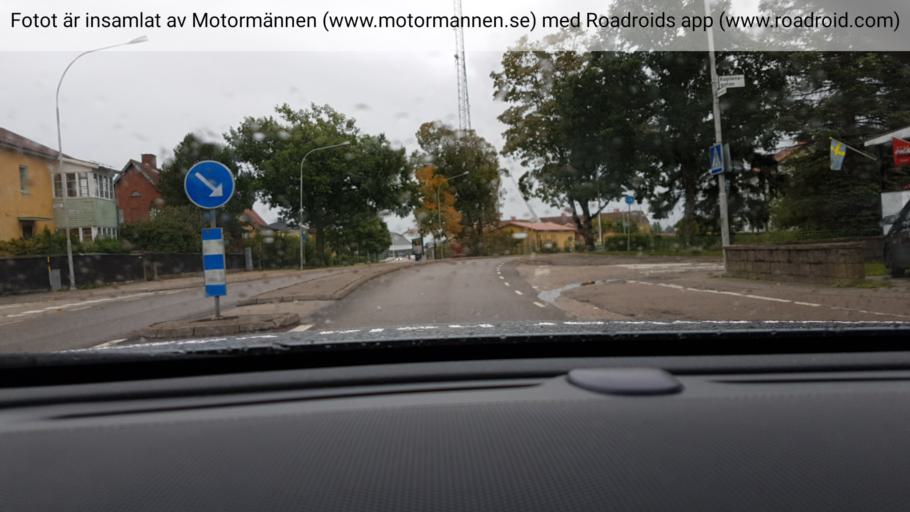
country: SE
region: Vaestra Goetaland
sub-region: Vanersborgs Kommun
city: Vanersborg
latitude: 58.3717
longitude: 12.3229
